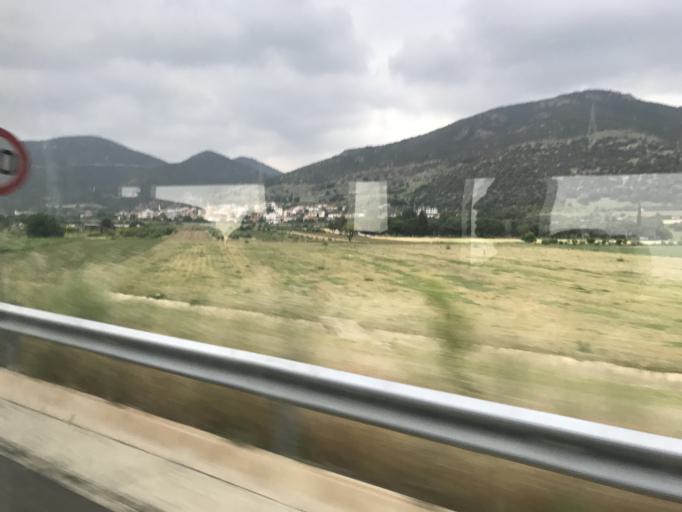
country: GR
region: East Macedonia and Thrace
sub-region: Nomos Rodopis
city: Iasmos
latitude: 41.1134
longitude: 25.1294
